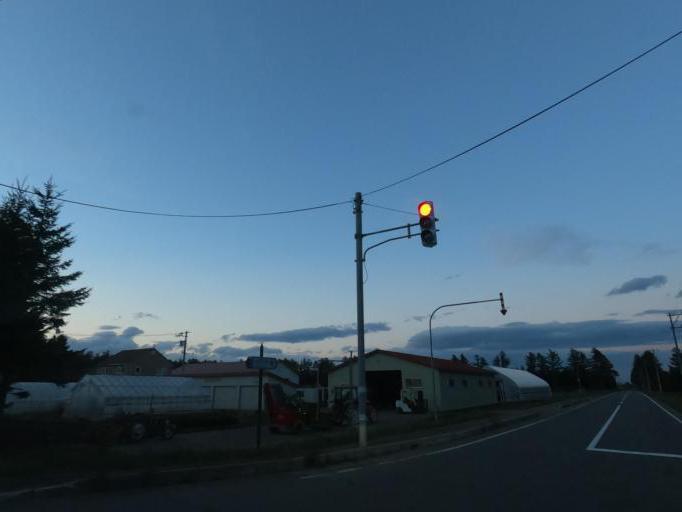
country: JP
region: Hokkaido
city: Obihiro
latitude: 42.6788
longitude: 143.1569
